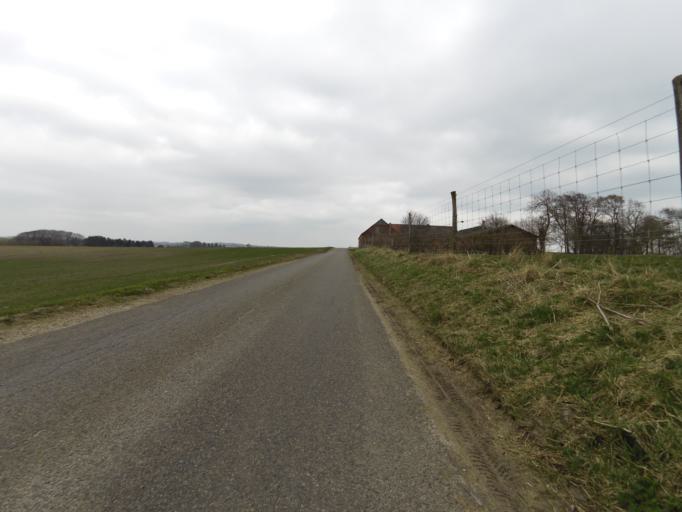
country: DK
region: Central Jutland
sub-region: Holstebro Kommune
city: Vinderup
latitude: 56.4256
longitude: 8.7191
